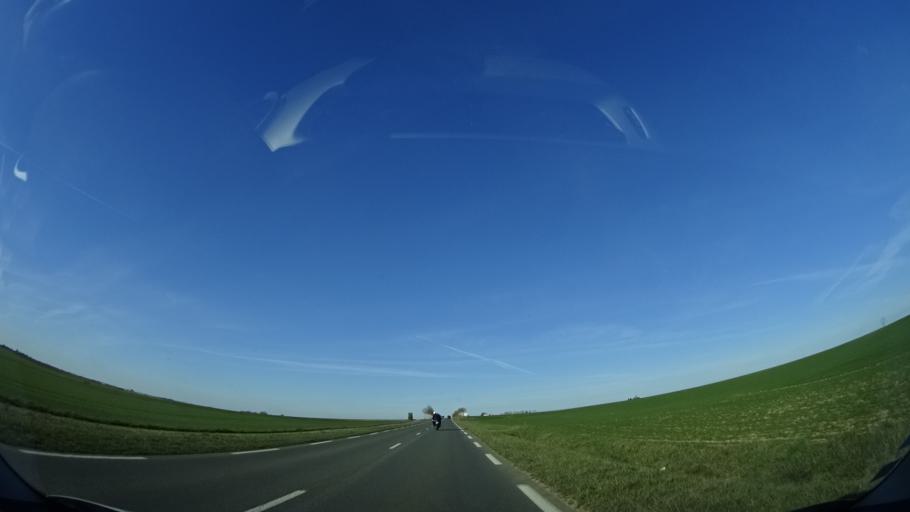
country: FR
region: Poitou-Charentes
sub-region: Departement de la Vienne
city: Avanton
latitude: 46.6848
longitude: 0.3254
